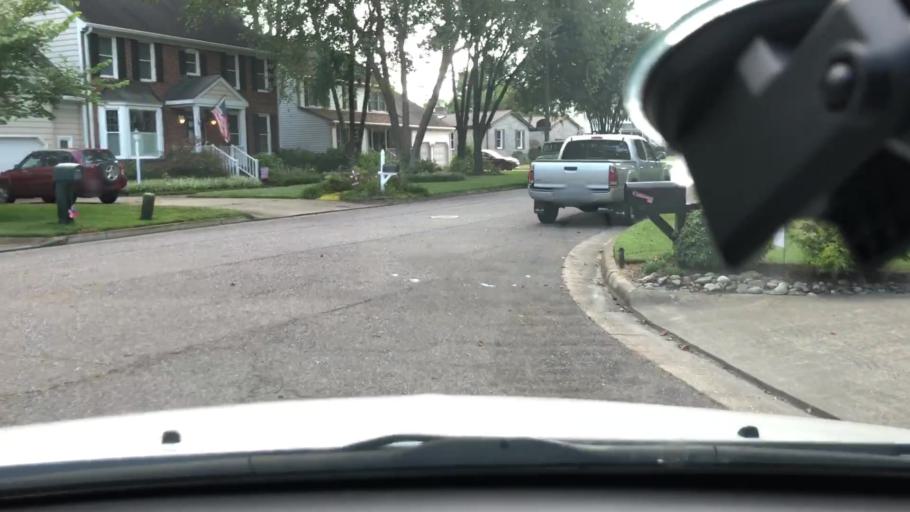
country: US
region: Virginia
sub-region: City of Chesapeake
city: Chesapeake
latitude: 36.7016
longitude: -76.2882
